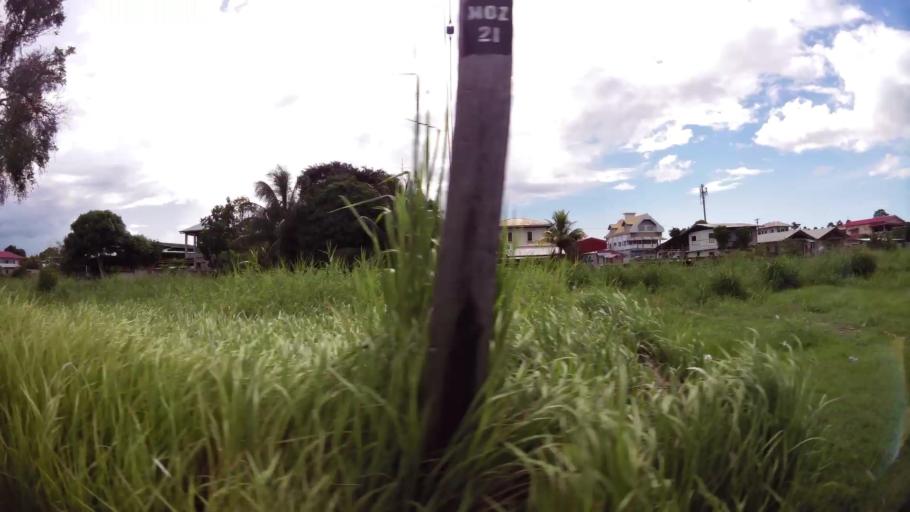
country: SR
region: Paramaribo
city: Paramaribo
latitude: 5.8501
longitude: -55.1511
